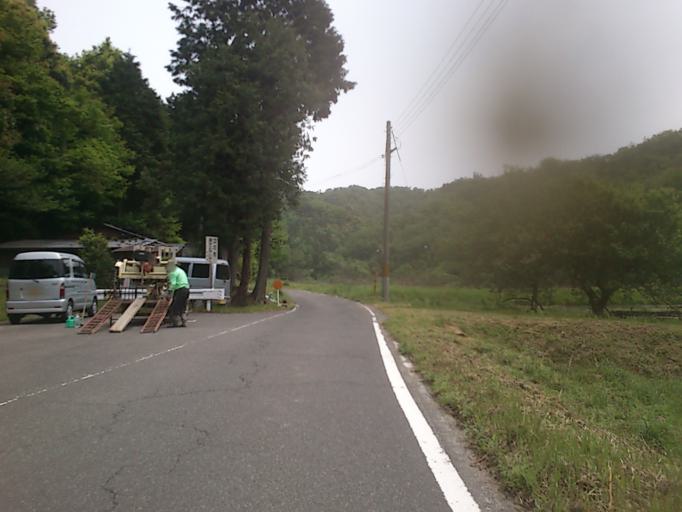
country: JP
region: Kyoto
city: Miyazu
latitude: 35.6049
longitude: 135.1064
